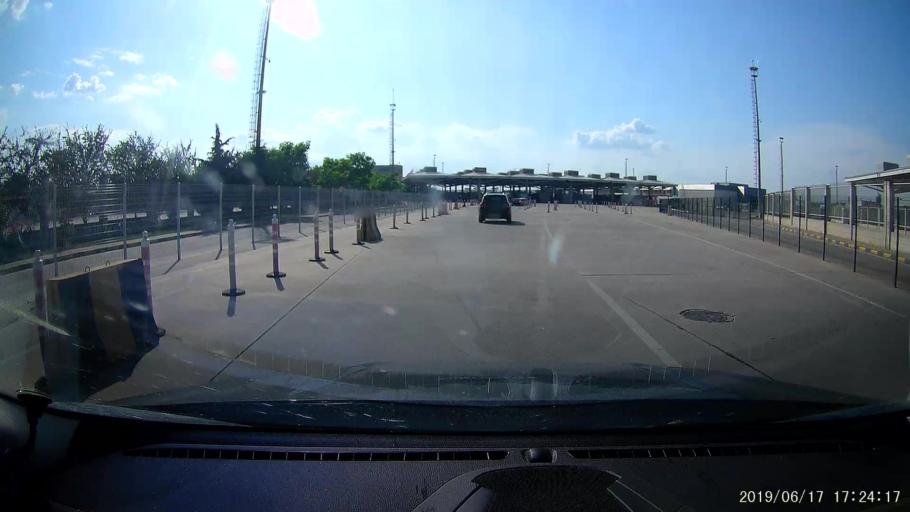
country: GR
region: East Macedonia and Thrace
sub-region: Nomos Evrou
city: Rizia
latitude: 41.7152
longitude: 26.3612
